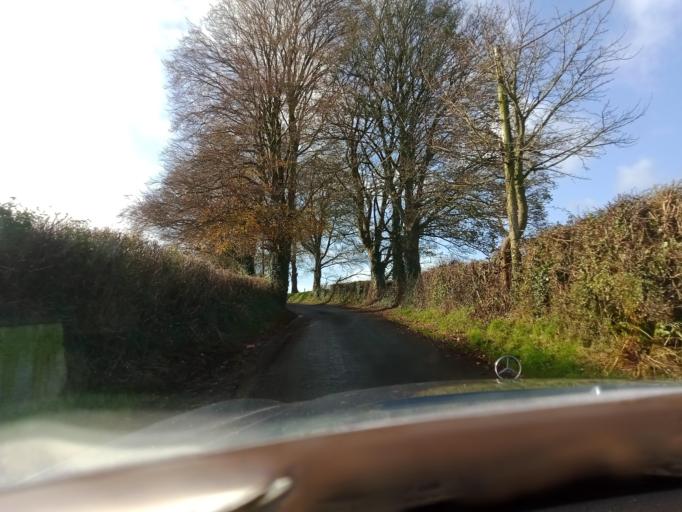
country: IE
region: Leinster
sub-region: Kilkenny
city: Mooncoin
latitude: 52.3328
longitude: -7.2698
